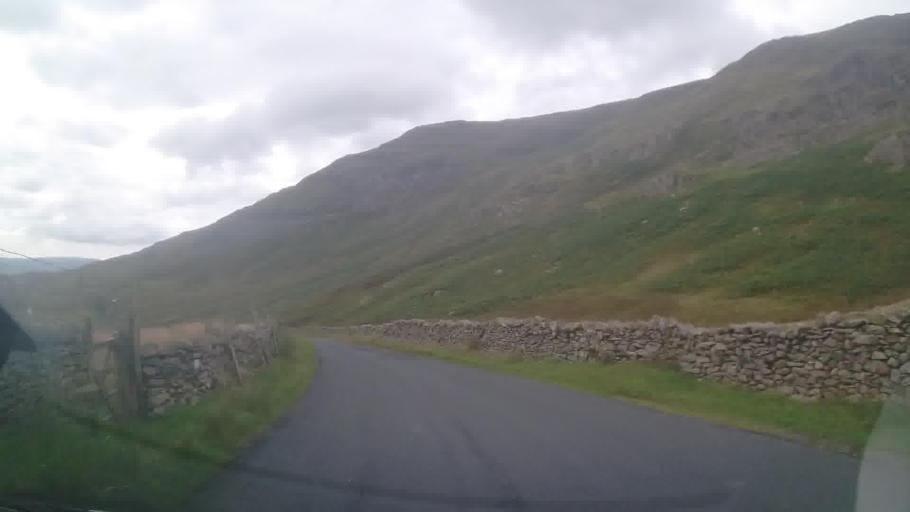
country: GB
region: England
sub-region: Cumbria
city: Ambleside
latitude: 54.4616
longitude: -2.9288
